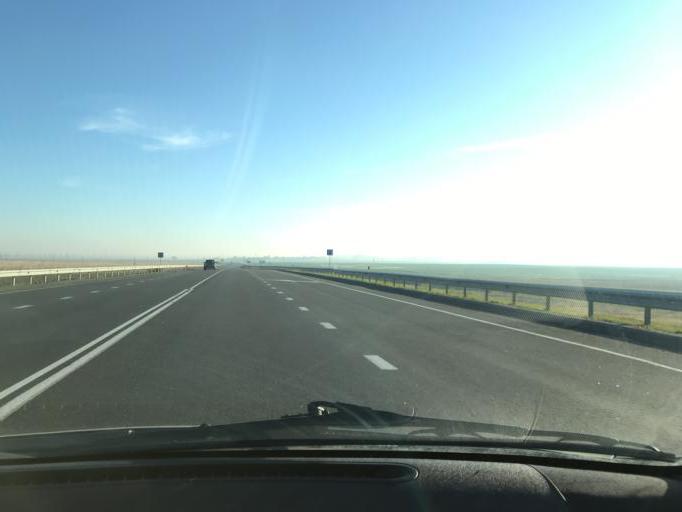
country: BY
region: Brest
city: Asnyezhytsy
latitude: 52.1848
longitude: 26.0814
